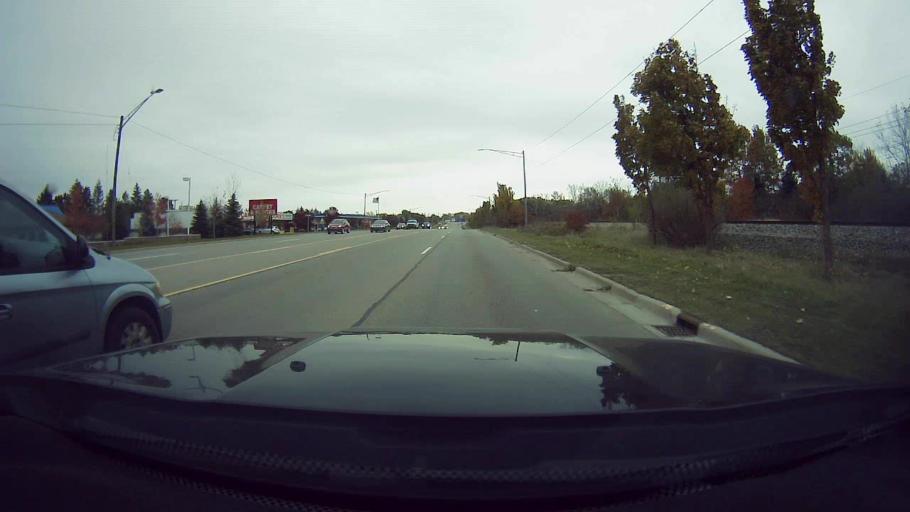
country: US
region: Michigan
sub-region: Oakland County
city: Waterford
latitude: 42.6774
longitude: -83.3627
